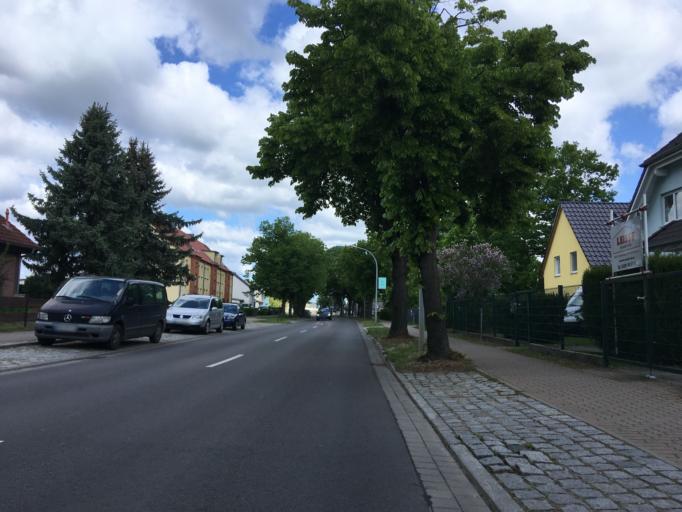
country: DE
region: Brandenburg
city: Oranienburg
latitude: 52.7639
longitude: 13.2545
